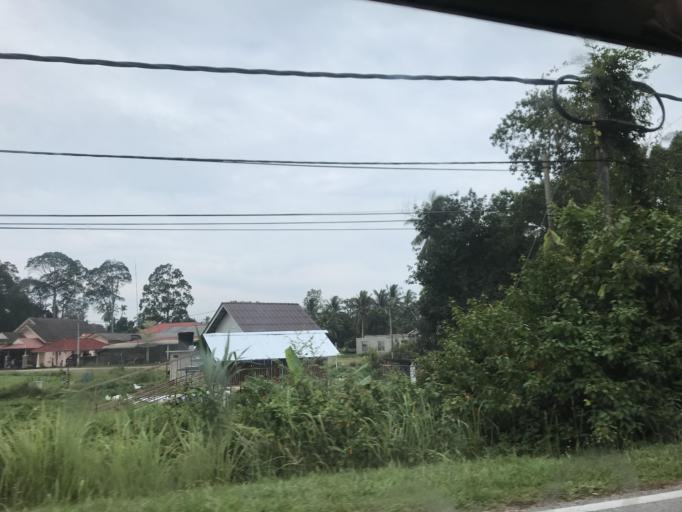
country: MY
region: Kelantan
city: Kota Bharu
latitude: 6.1666
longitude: 102.2278
